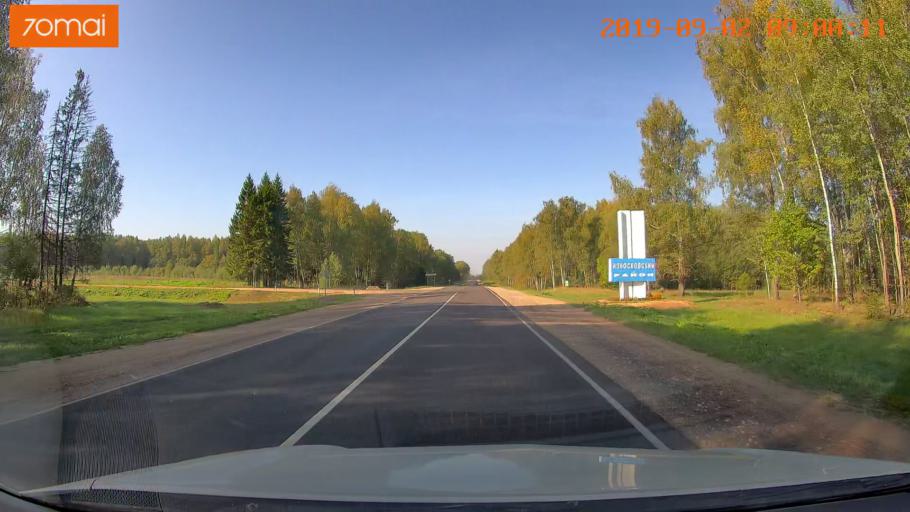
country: RU
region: Kaluga
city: Myatlevo
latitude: 54.9148
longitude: 35.7131
